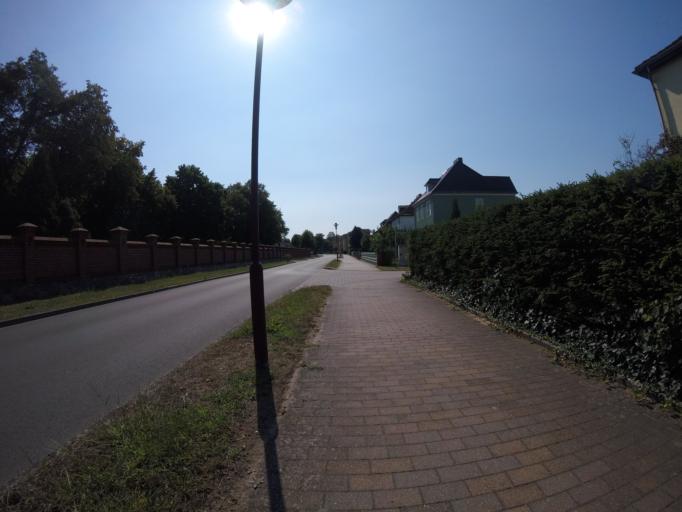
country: DE
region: Brandenburg
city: Mullrose
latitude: 52.2441
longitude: 14.4100
